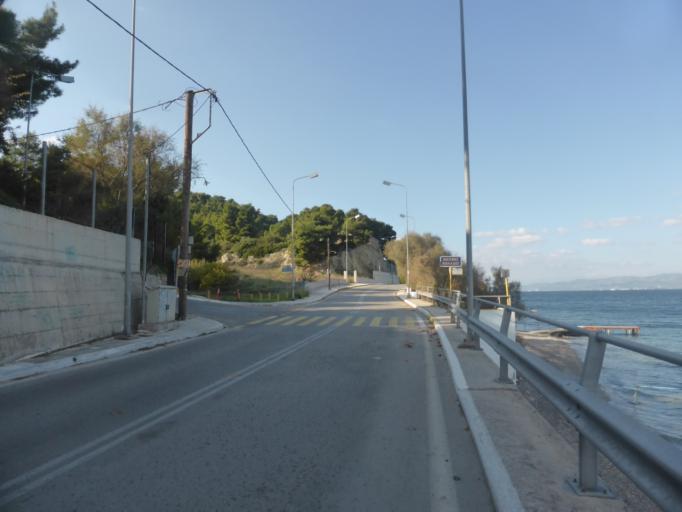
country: GR
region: Attica
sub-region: Nomarchia Anatolikis Attikis
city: Kalamos
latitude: 38.3093
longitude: 23.8500
